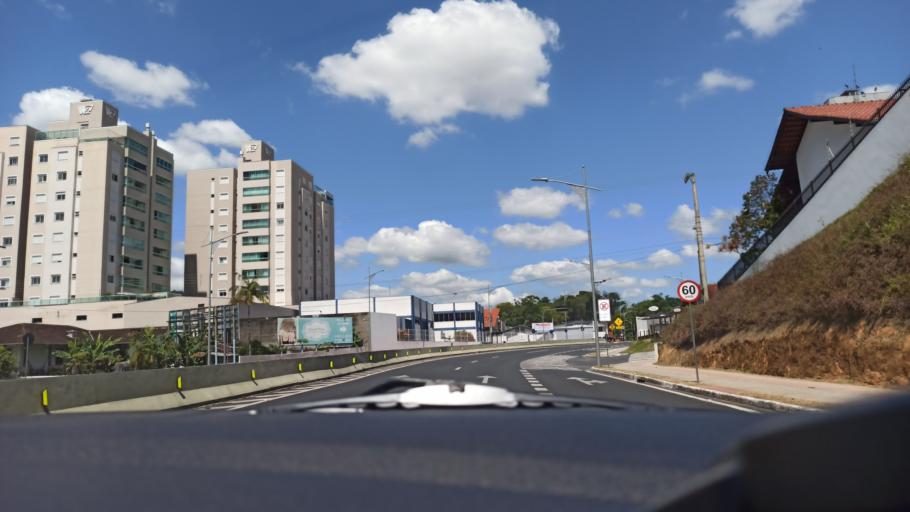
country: BR
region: Santa Catarina
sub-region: Blumenau
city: Blumenau
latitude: -26.9159
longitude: -49.0974
